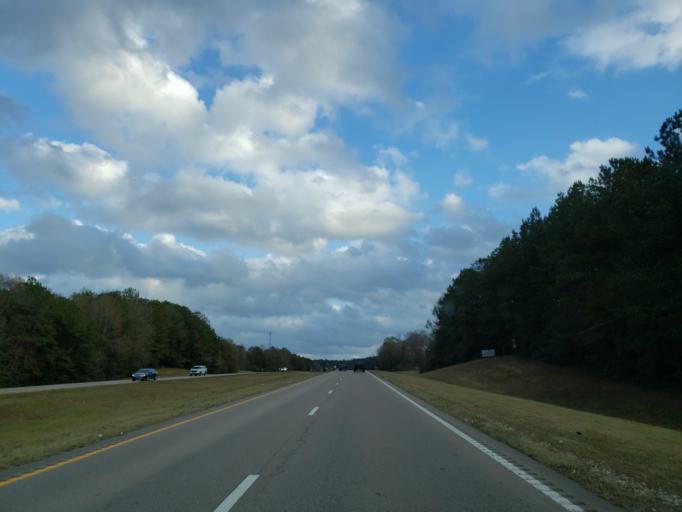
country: US
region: Mississippi
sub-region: Perry County
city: New Augusta
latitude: 31.1627
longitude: -88.9292
